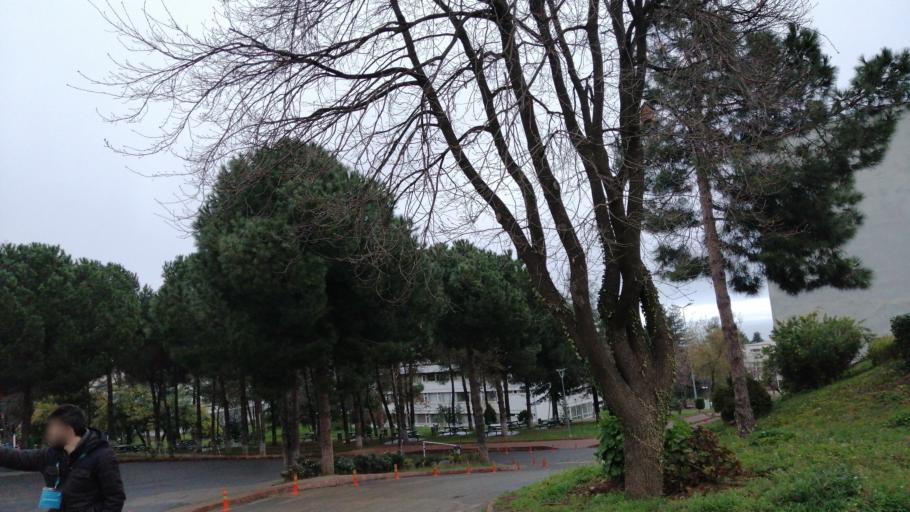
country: TR
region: Trabzon
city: Trabzon
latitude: 40.9914
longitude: 39.7754
